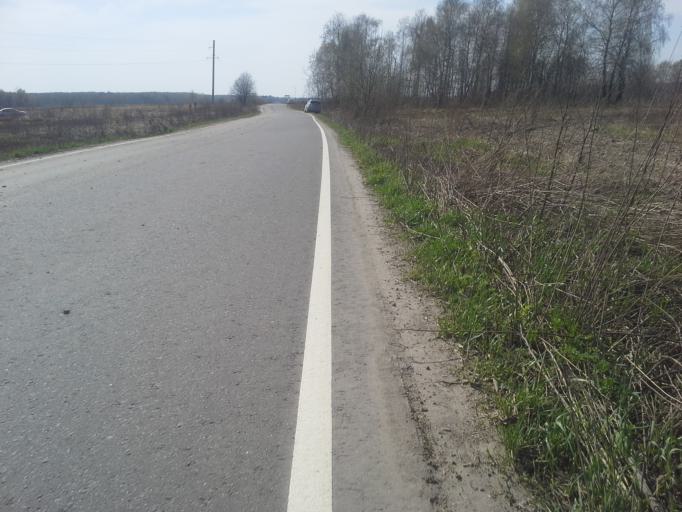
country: RU
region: Moskovskaya
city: Dubrovitsy
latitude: 55.4726
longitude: 37.4551
